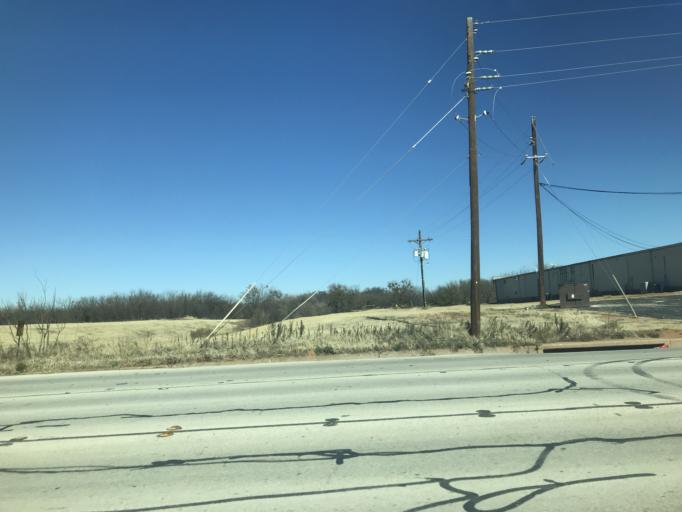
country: US
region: Texas
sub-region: Taylor County
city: Abilene
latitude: 32.4441
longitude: -99.7977
